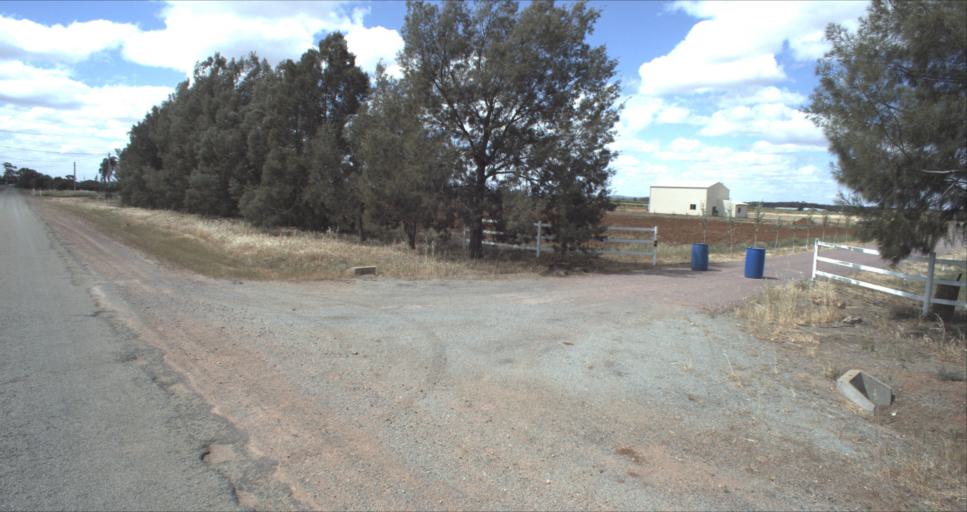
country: AU
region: New South Wales
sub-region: Leeton
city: Leeton
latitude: -34.5852
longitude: 146.3962
